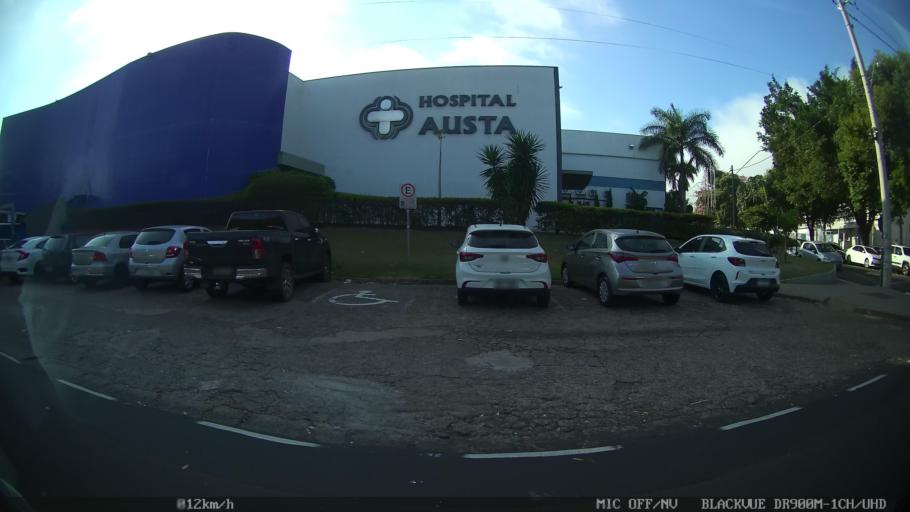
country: BR
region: Sao Paulo
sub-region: Sao Jose Do Rio Preto
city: Sao Jose do Rio Preto
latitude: -20.8232
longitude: -49.3655
